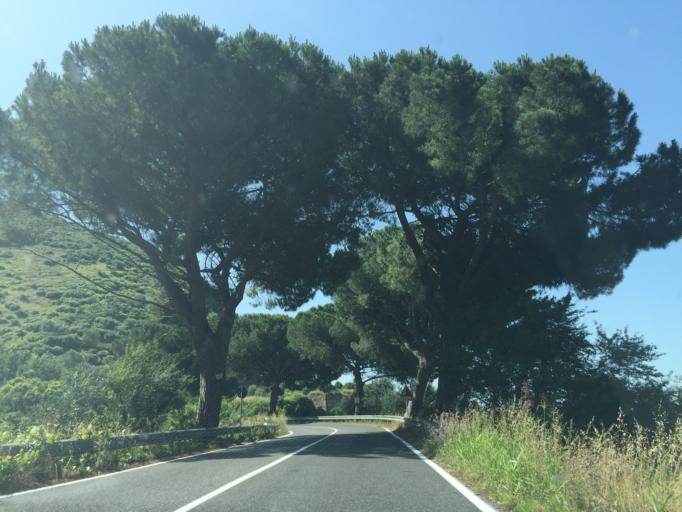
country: IT
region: Tuscany
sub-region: Province of Pisa
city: San Giuliano Terme
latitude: 43.7636
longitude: 10.4454
